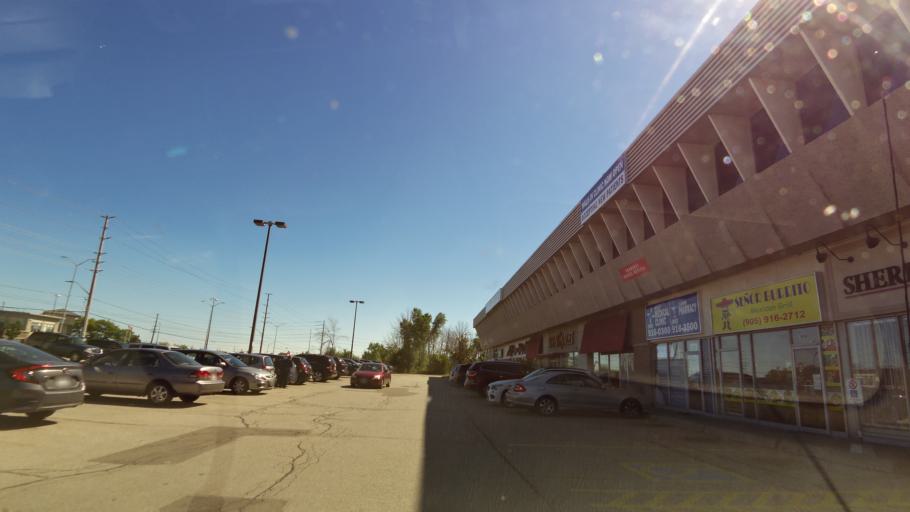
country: CA
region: Ontario
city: Mississauga
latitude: 43.5264
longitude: -79.6522
